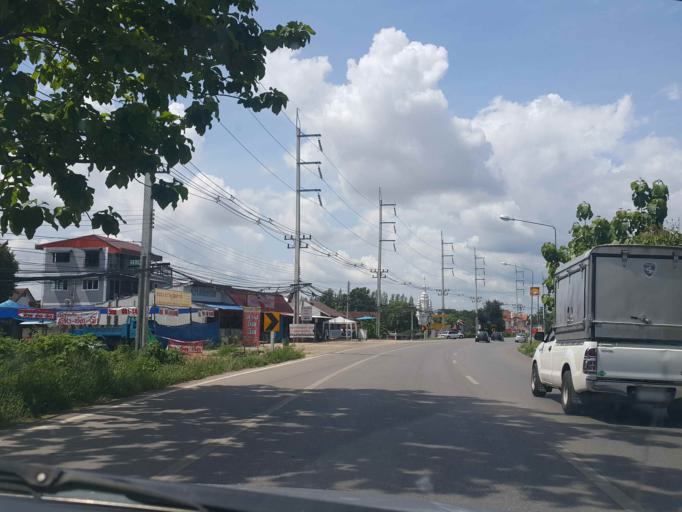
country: TH
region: Phayao
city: Phayao
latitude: 19.1588
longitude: 99.9144
